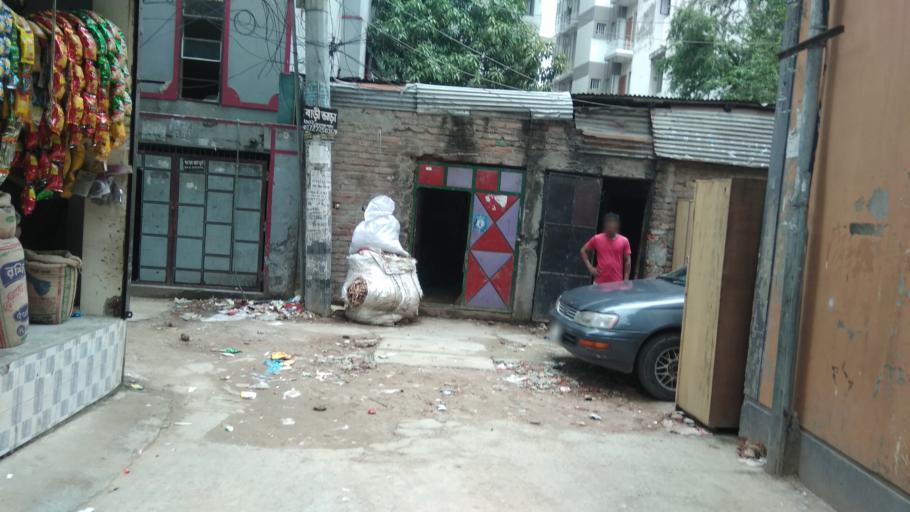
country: BD
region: Dhaka
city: Azimpur
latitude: 23.8032
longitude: 90.3721
